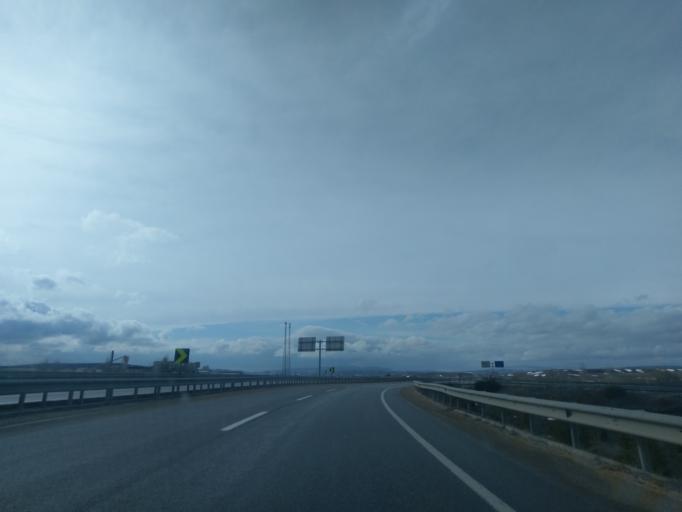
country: TR
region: Eskisehir
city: Inonu
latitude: 39.7086
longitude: 30.1596
